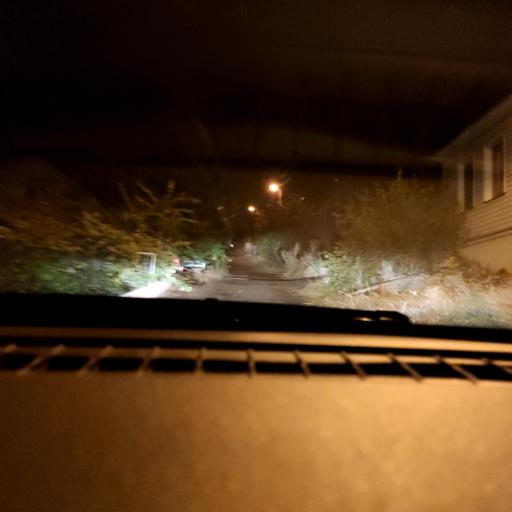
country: RU
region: Voronezj
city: Voronezh
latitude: 51.6419
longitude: 39.1928
